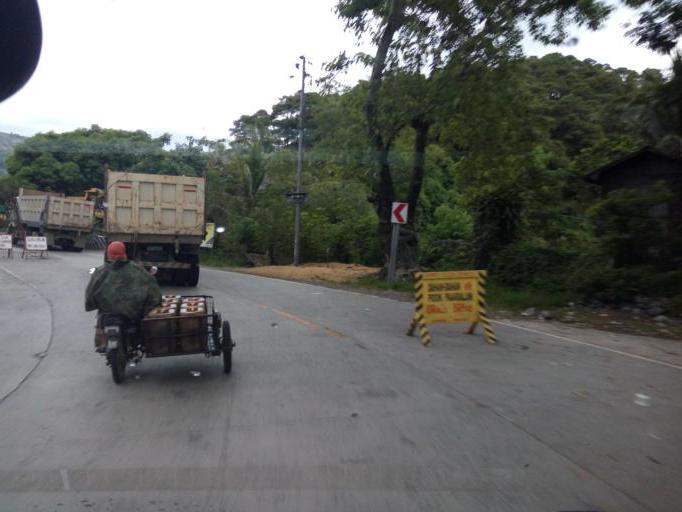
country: PH
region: Cagayan Valley
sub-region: Province of Nueva Vizcaya
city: Santa Fe
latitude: 16.0733
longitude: 120.9427
